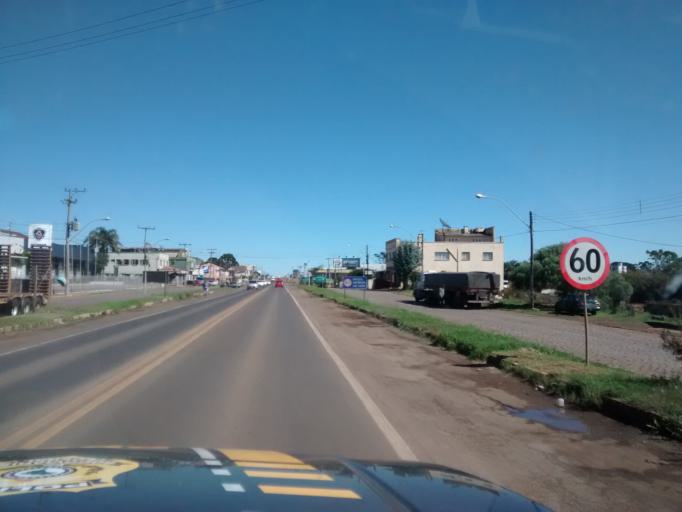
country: BR
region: Rio Grande do Sul
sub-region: Vacaria
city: Vacaria
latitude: -28.5074
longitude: -50.9273
